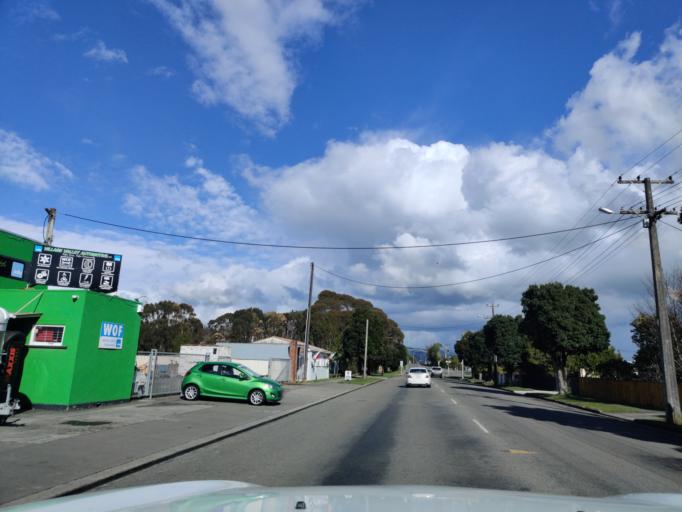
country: NZ
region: Manawatu-Wanganui
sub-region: Palmerston North City
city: Palmerston North
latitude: -40.2938
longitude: 175.7538
